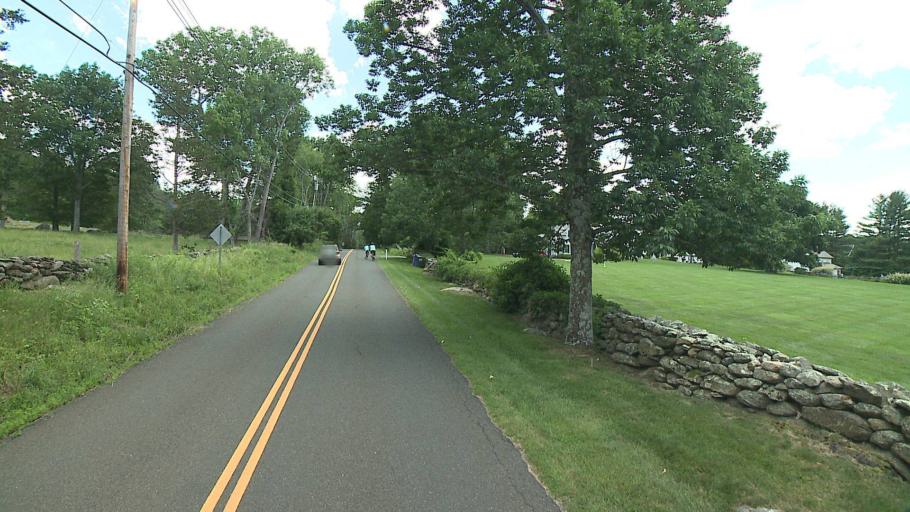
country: US
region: Connecticut
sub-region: Litchfield County
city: New Preston
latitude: 41.7067
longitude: -73.3770
